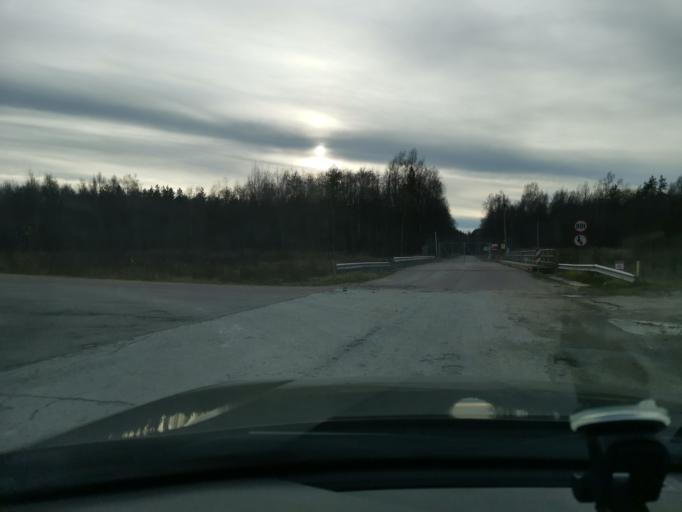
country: EE
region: Ida-Virumaa
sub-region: Sillamaee linn
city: Sillamae
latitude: 59.2657
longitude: 27.8988
